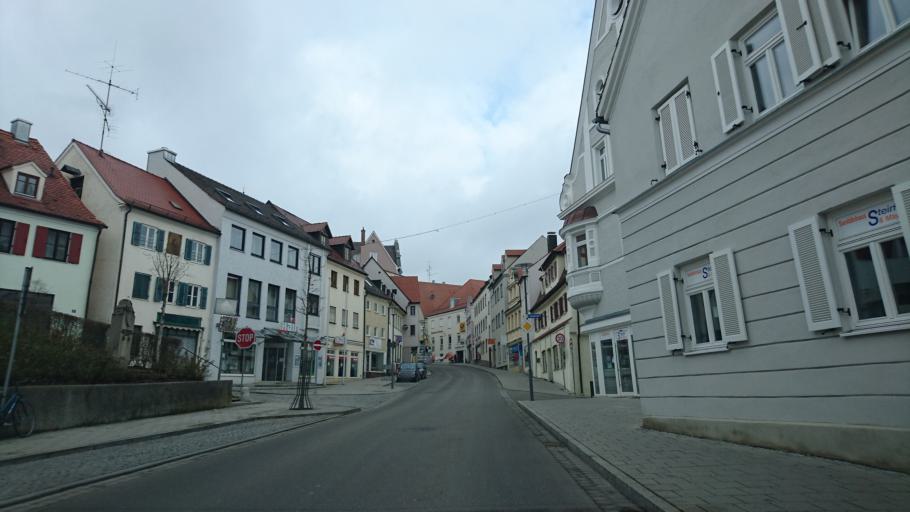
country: DE
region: Bavaria
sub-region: Swabia
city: Dillingen an der Donau
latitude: 48.5767
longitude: 10.4966
